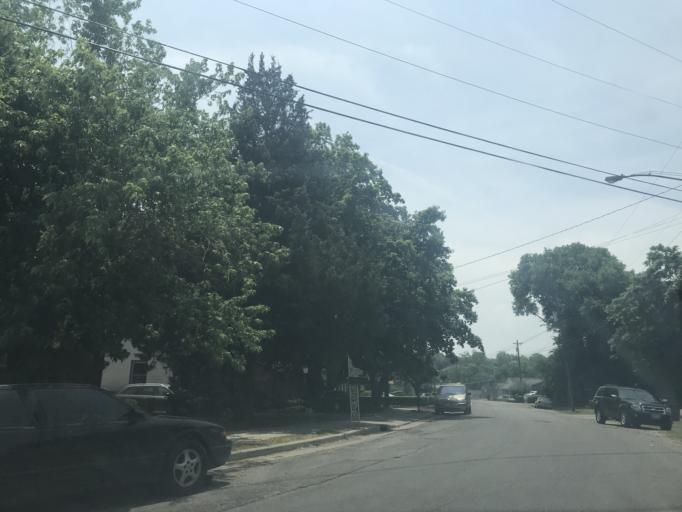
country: US
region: Tennessee
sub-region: Davidson County
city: Nashville
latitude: 36.1915
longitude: -86.8117
